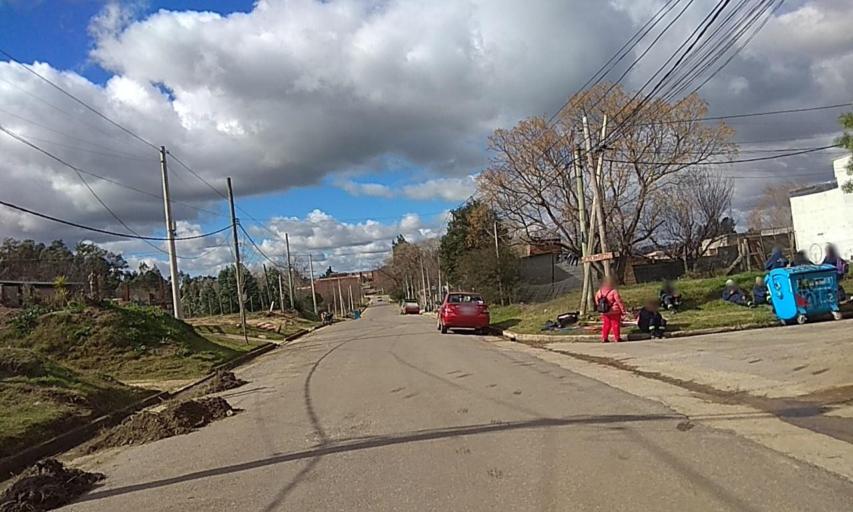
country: UY
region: Florida
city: Florida
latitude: -34.0871
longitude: -56.2287
